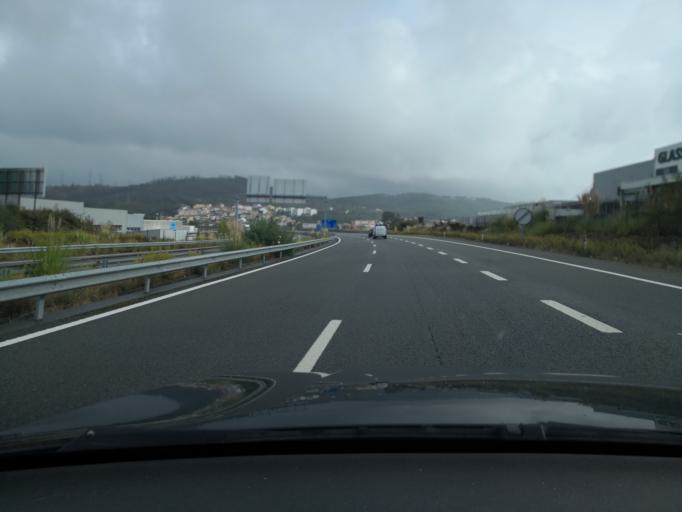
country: PT
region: Porto
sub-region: Valongo
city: Alfena
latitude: 41.2317
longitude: -8.5368
